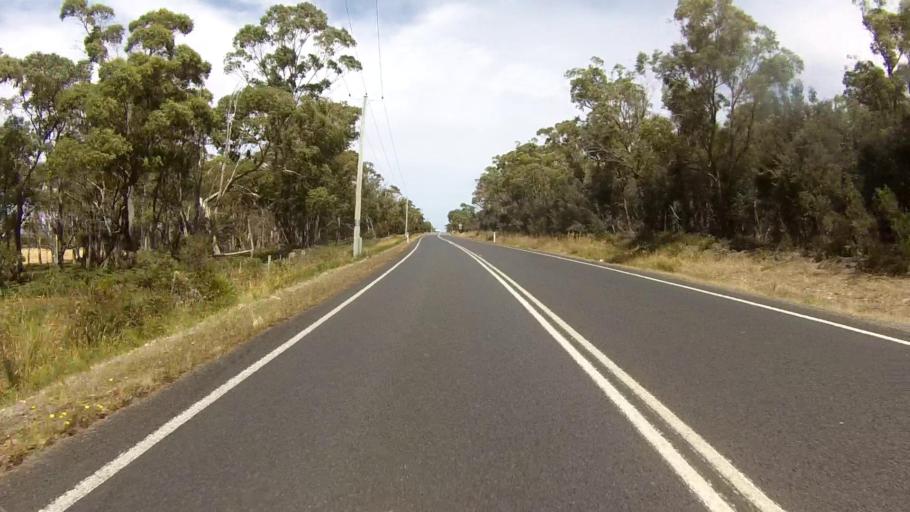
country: AU
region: Tasmania
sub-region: Clarence
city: Sandford
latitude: -43.0014
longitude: 147.4950
